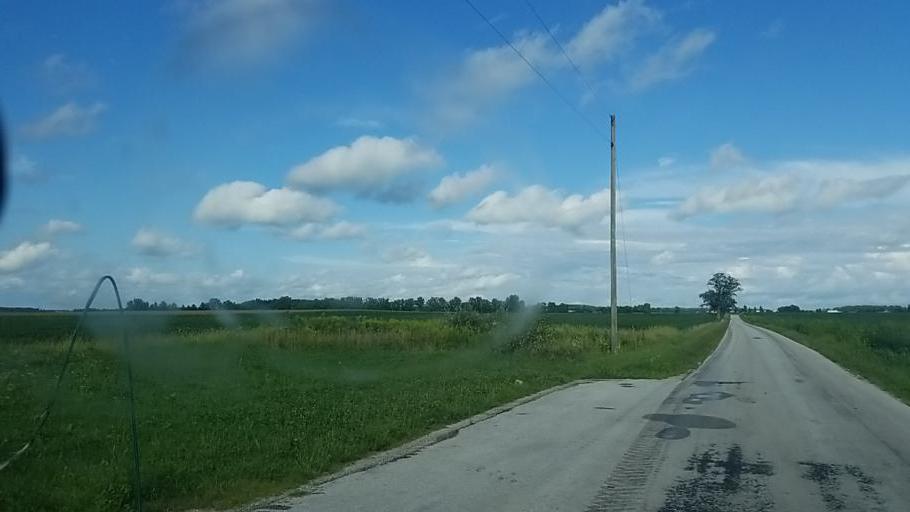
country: US
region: Ohio
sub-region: Hardin County
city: Forest
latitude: 40.7451
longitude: -83.5157
